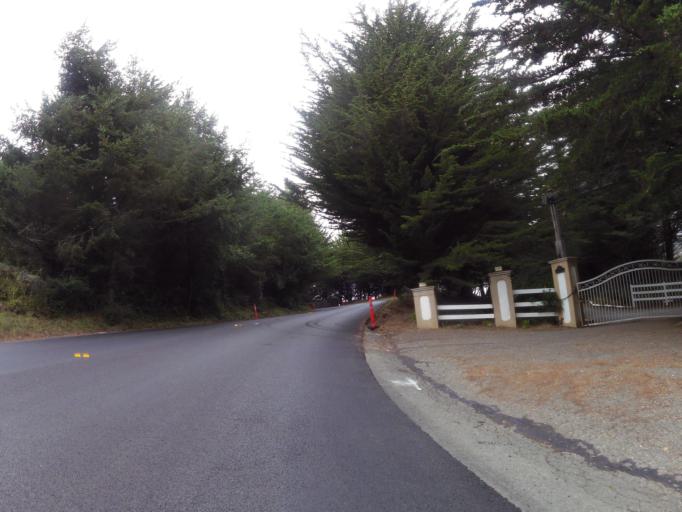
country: US
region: California
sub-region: Sonoma County
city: Monte Rio
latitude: 38.4320
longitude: -123.1040
